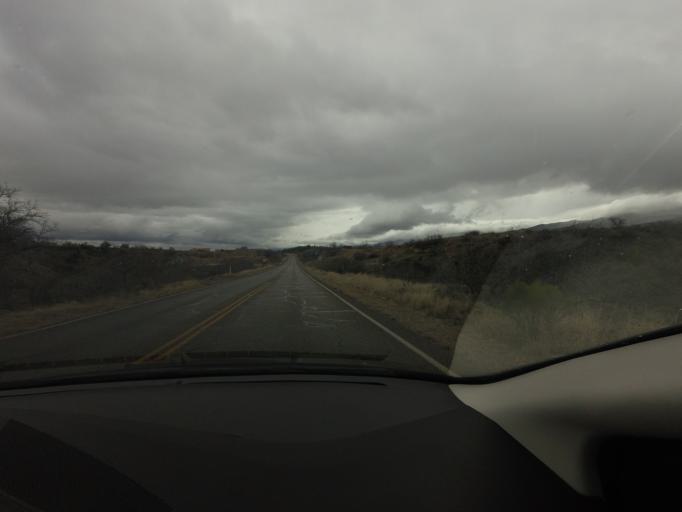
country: US
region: Arizona
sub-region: Yavapai County
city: Clarkdale
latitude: 34.7575
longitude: -112.0375
